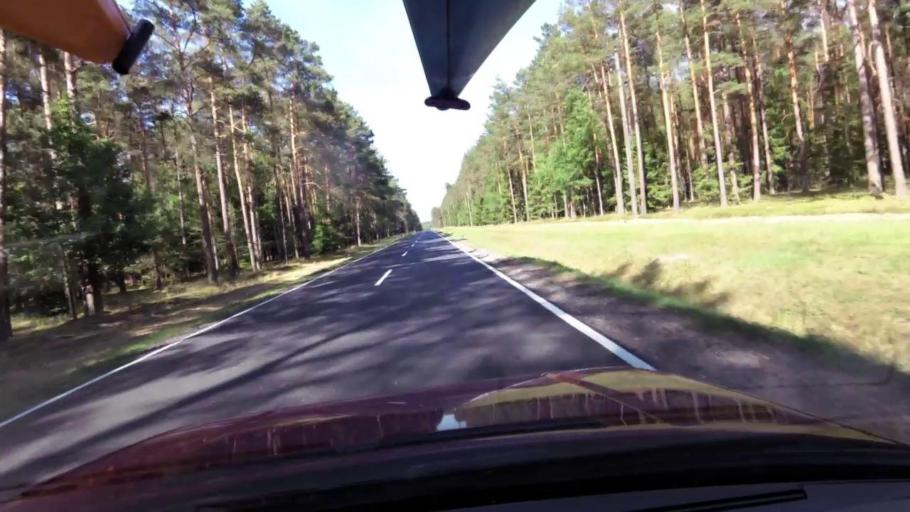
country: PL
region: Pomeranian Voivodeship
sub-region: Powiat bytowski
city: Trzebielino
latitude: 54.1374
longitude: 17.0220
